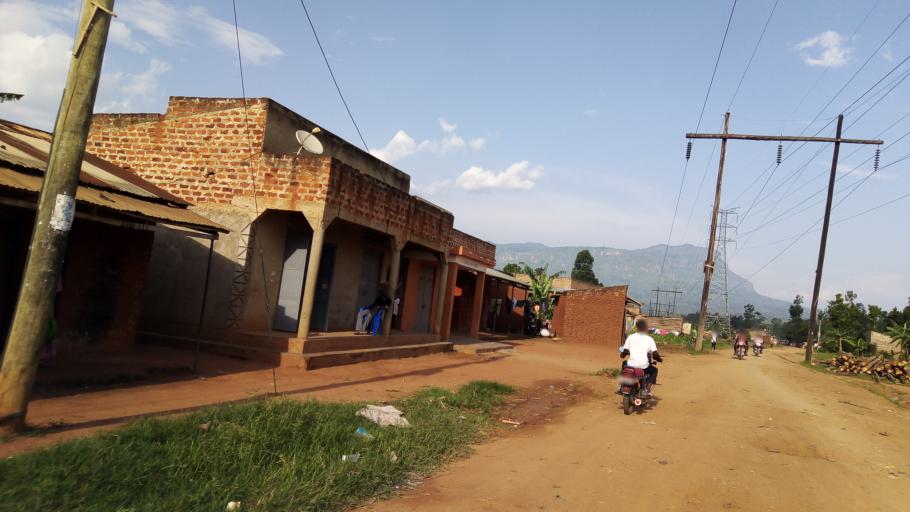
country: UG
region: Eastern Region
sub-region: Mbale District
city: Mbale
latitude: 1.0581
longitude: 34.1576
